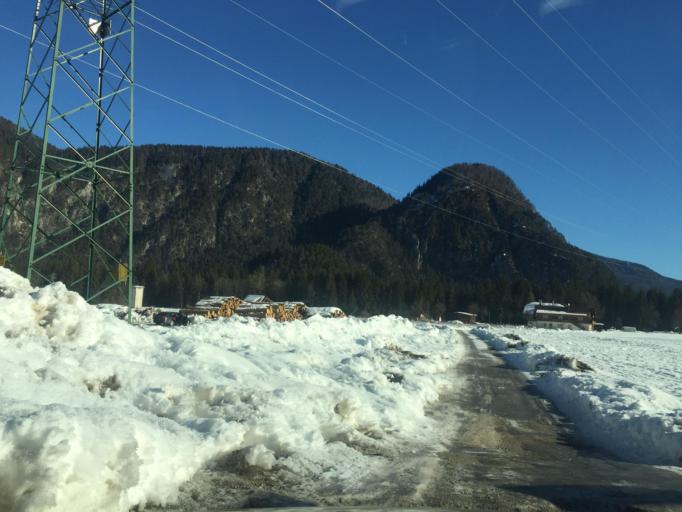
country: IT
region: Friuli Venezia Giulia
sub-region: Provincia di Udine
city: Malborghetto
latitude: 46.4988
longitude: 13.4860
